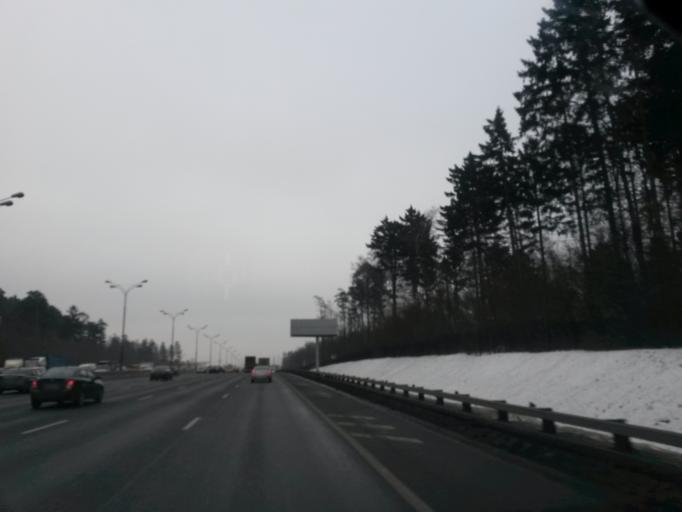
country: RU
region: Moscow
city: Yasenevo
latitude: 55.5858
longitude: 37.5521
